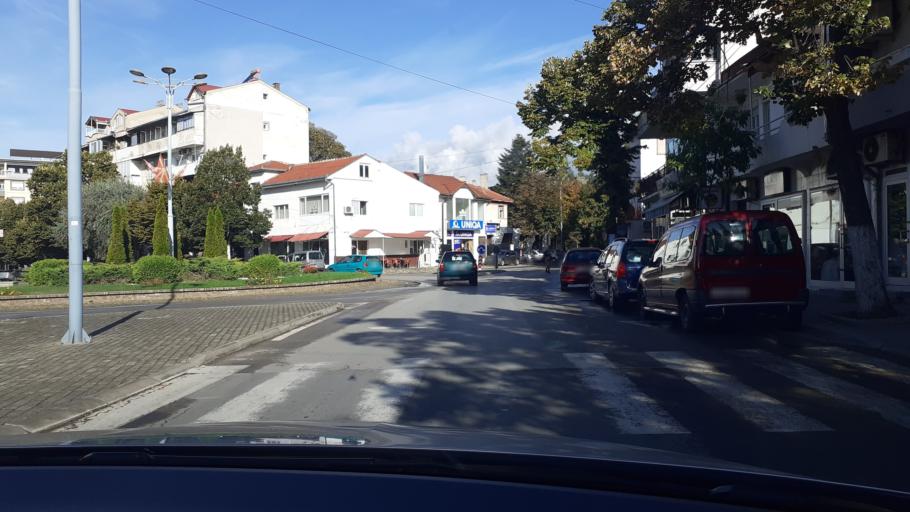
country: MK
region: Kocani
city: Kochani
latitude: 41.9144
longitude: 22.4141
